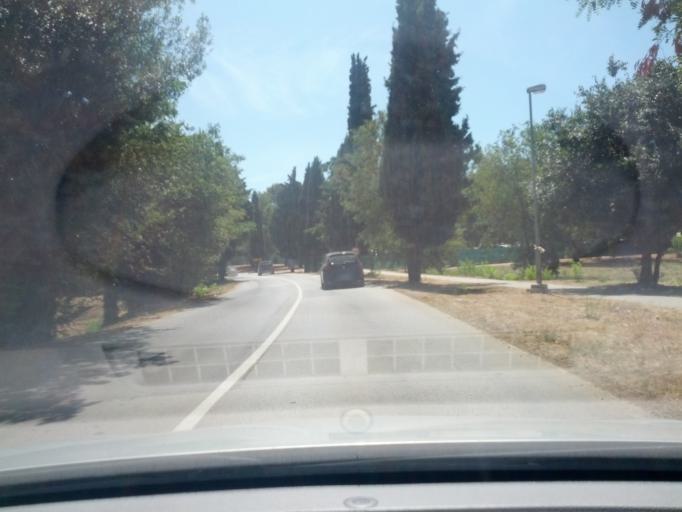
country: HR
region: Istarska
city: Fazana
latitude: 44.9206
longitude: 13.8082
